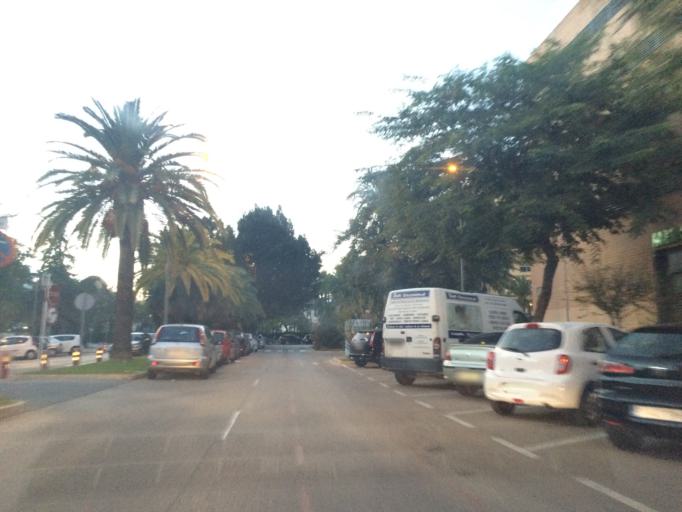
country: ES
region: Valencia
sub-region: Provincia de Alicante
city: Denia
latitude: 38.8350
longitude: 0.1045
